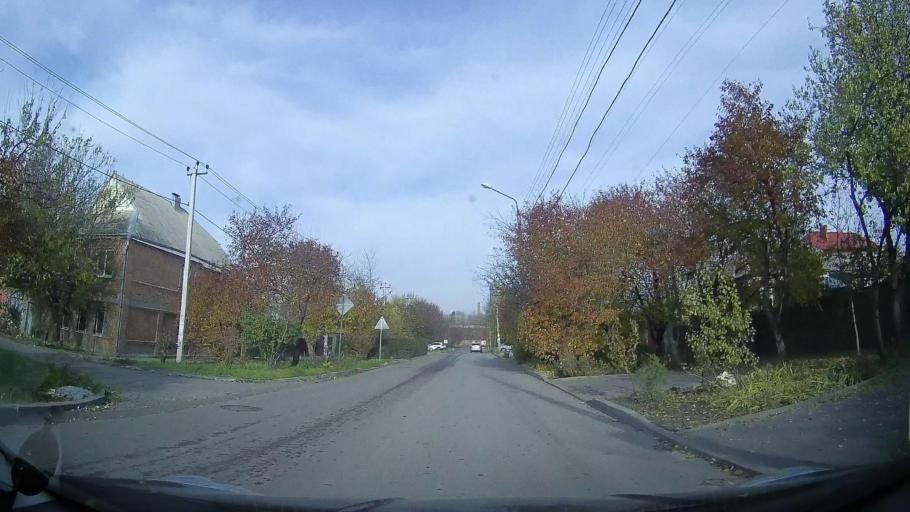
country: RU
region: Rostov
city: Severnyy
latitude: 47.2638
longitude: 39.7240
